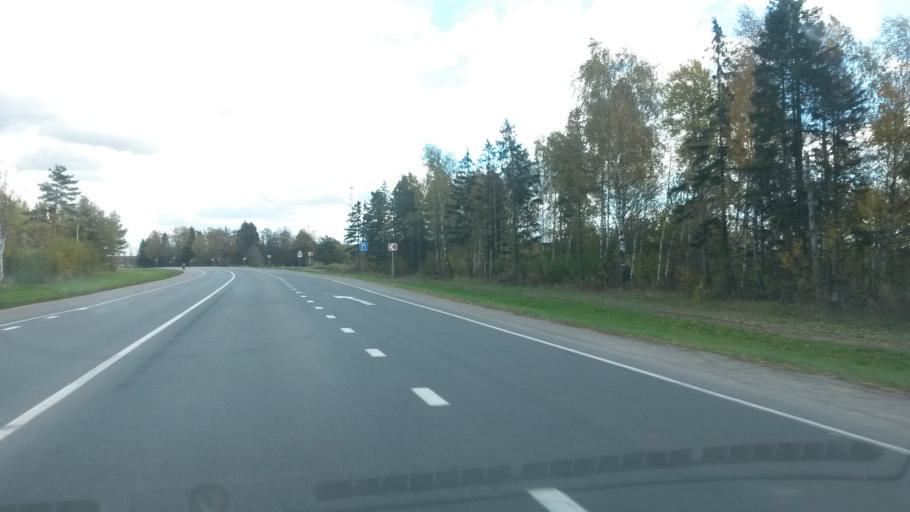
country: RU
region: Jaroslavl
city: Tunoshna
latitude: 57.5355
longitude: 40.0270
